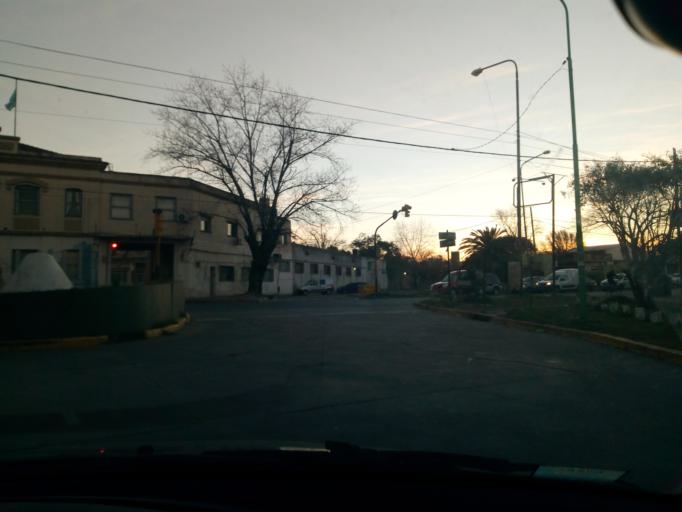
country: AR
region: Buenos Aires
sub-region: Partido de La Plata
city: La Plata
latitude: -34.8997
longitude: -57.9367
